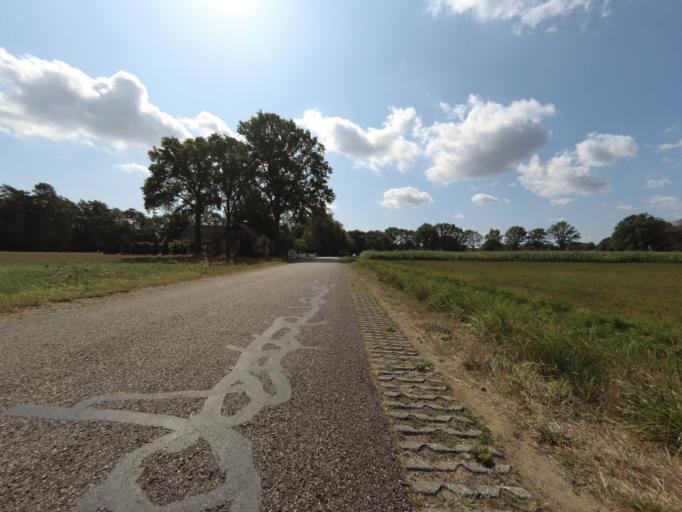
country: NL
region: Overijssel
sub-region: Gemeente Oldenzaal
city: Oldenzaal
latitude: 52.2998
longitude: 6.8802
